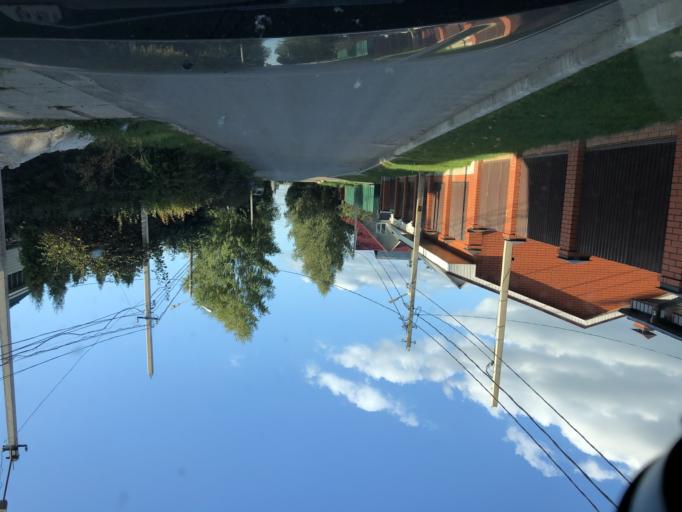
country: RU
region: Tula
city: Kosaya Gora
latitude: 54.1778
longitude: 37.5436
